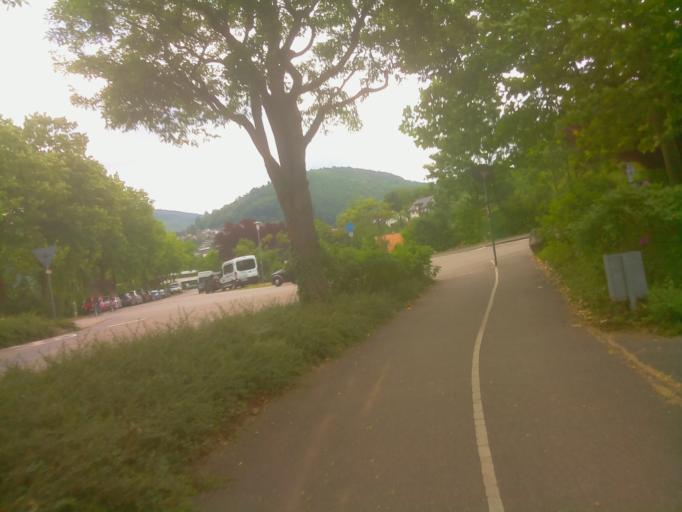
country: DE
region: Baden-Wuerttemberg
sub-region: Karlsruhe Region
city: Eberbach
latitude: 49.4622
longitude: 8.9752
